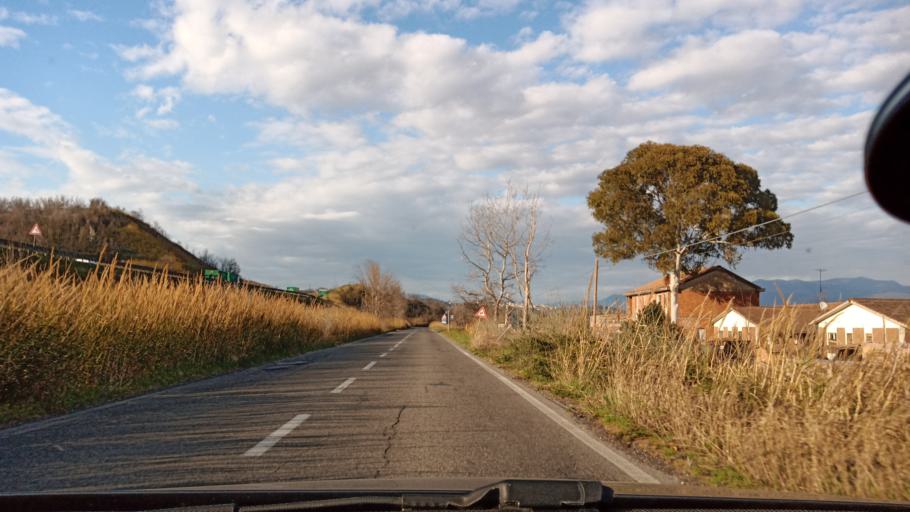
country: IT
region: Latium
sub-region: Citta metropolitana di Roma Capitale
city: Civitella San Paolo
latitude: 42.1927
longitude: 12.6044
